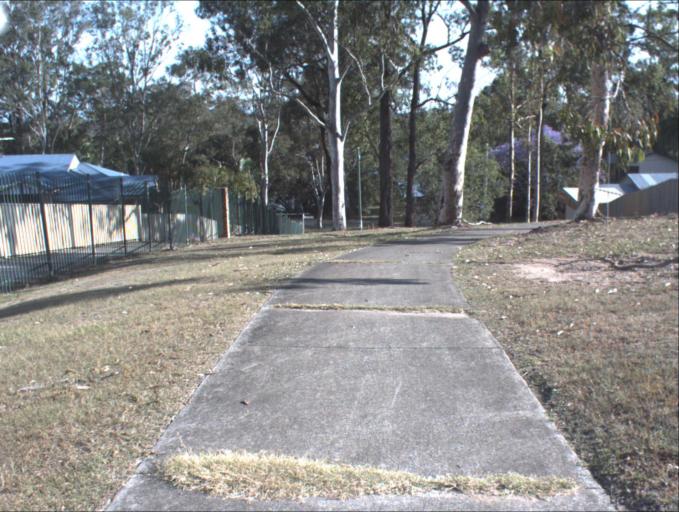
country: AU
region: Queensland
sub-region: Logan
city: Beenleigh
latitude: -27.6789
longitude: 153.2054
